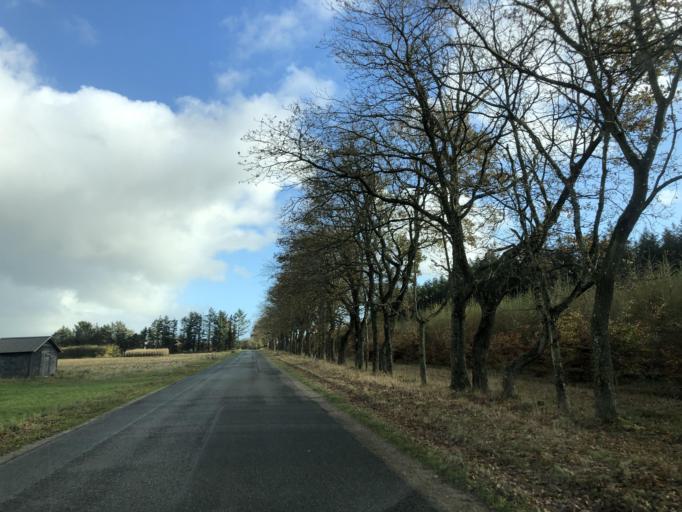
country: DK
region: Central Jutland
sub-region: Ringkobing-Skjern Kommune
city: Ringkobing
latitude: 56.1377
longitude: 8.3394
